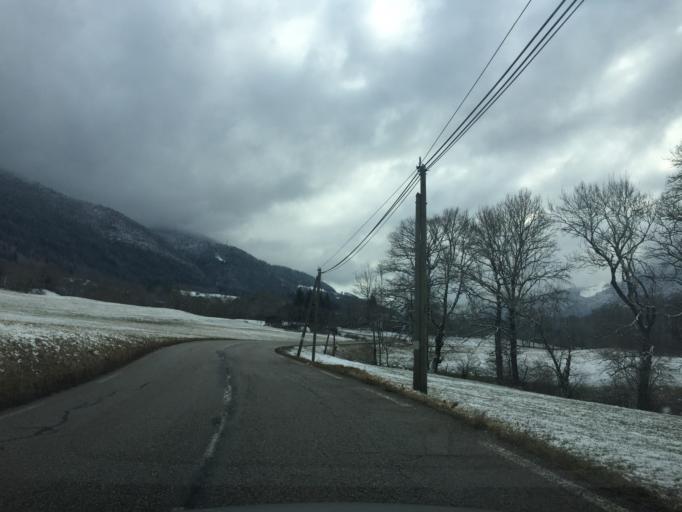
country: FR
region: Rhone-Alpes
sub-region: Departement de la Haute-Savoie
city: Gruffy
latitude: 45.7074
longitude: 6.1166
